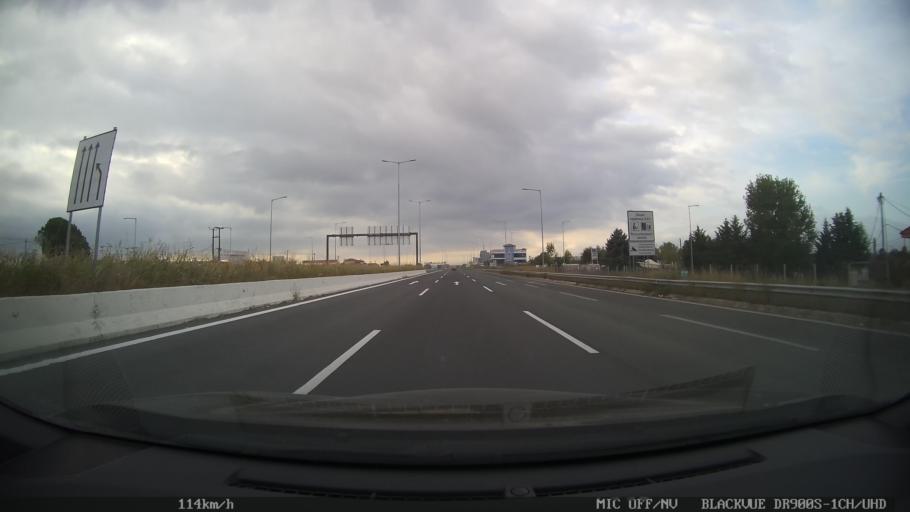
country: GR
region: Central Macedonia
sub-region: Nomos Pierias
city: Peristasi
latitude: 40.2538
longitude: 22.5321
